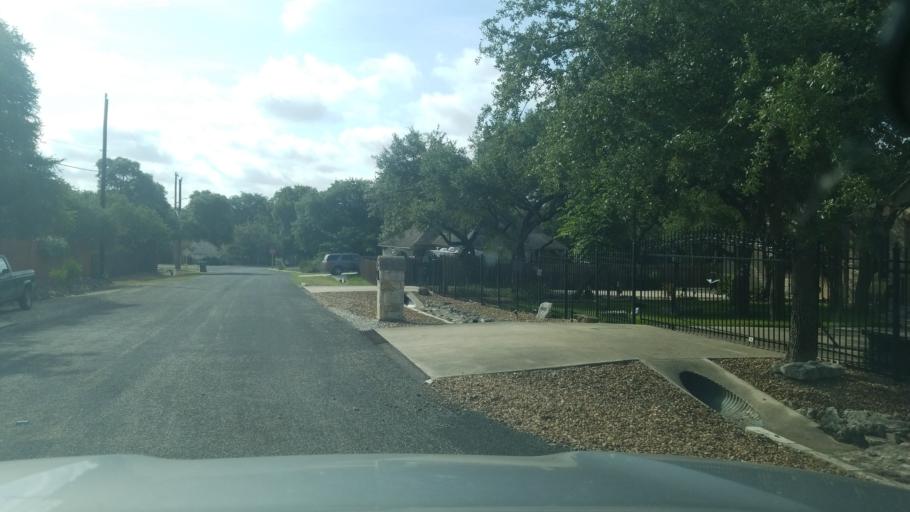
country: US
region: Texas
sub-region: Bexar County
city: Timberwood Park
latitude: 29.6959
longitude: -98.4998
